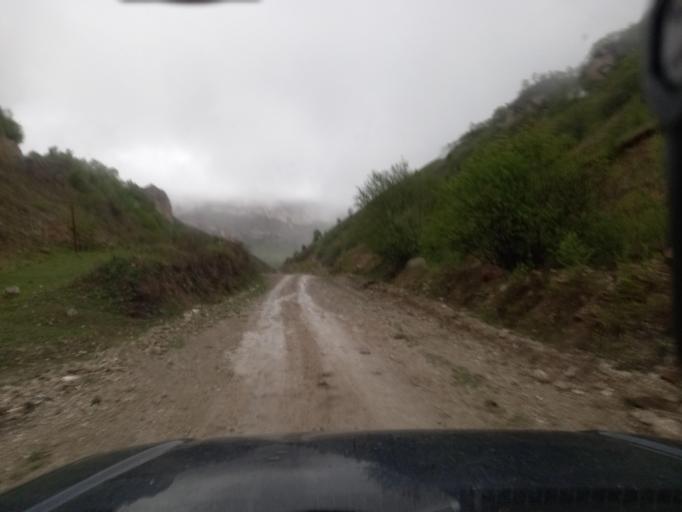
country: RU
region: Kabardino-Balkariya
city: Zhankhoteko
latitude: 43.4986
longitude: 43.1541
